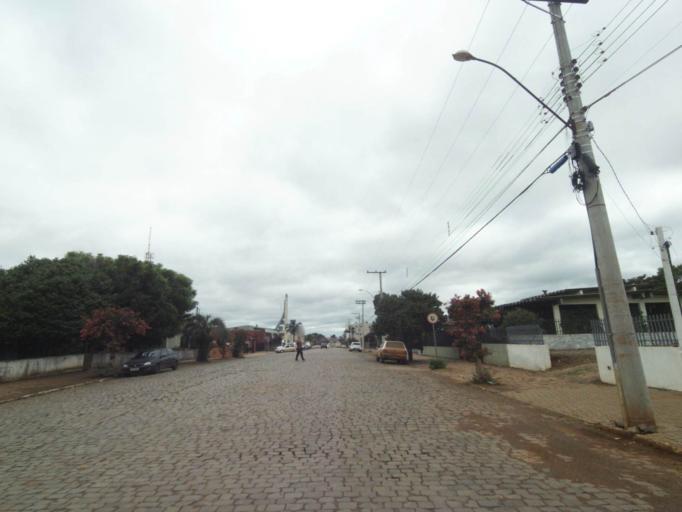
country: BR
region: Rio Grande do Sul
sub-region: Lagoa Vermelha
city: Lagoa Vermelha
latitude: -28.2159
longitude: -51.5190
